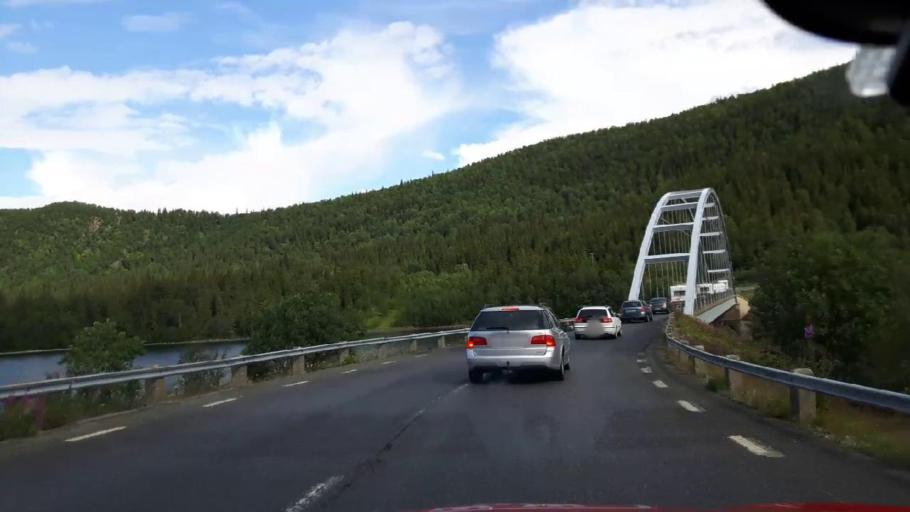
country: SE
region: Vaesterbotten
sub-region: Vilhelmina Kommun
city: Sjoberg
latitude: 65.0308
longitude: 15.1386
